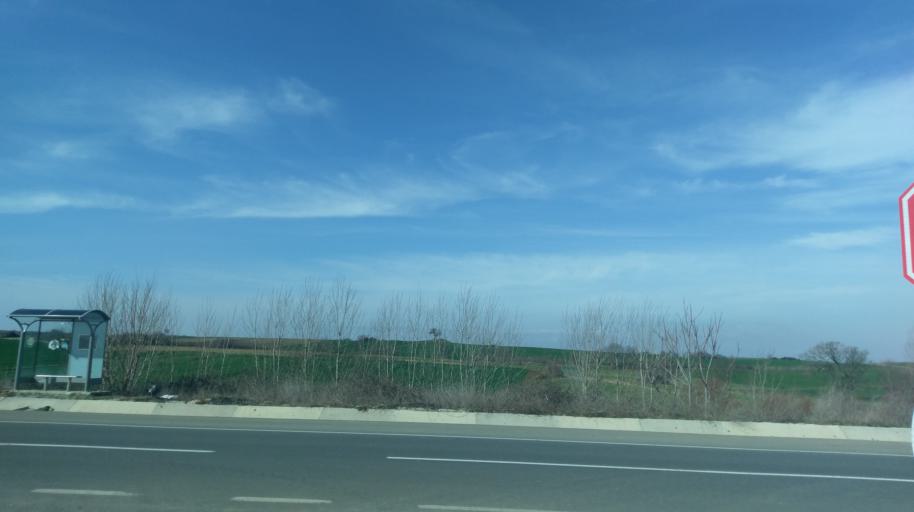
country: TR
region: Edirne
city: Kesan
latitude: 40.9904
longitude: 26.6377
